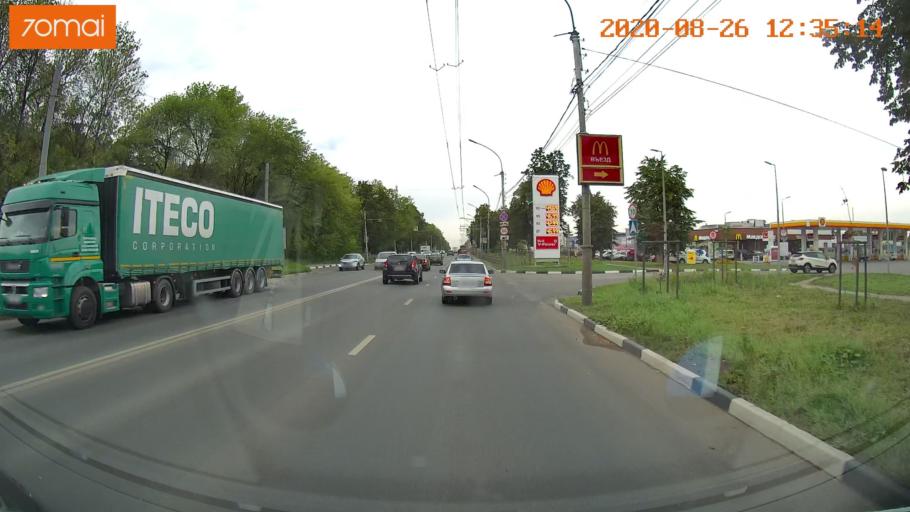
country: RU
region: Rjazan
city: Ryazan'
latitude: 54.5942
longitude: 39.7688
